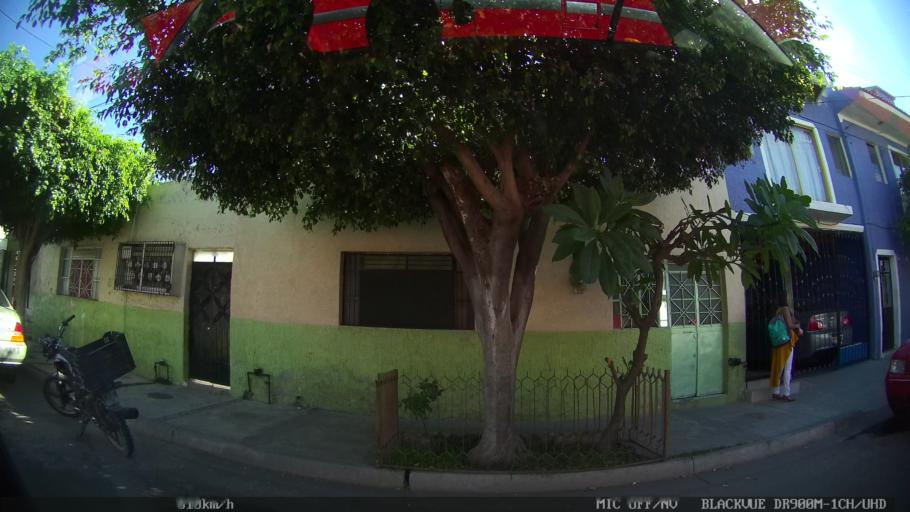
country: MX
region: Jalisco
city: Tlaquepaque
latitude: 20.6732
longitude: -103.2815
